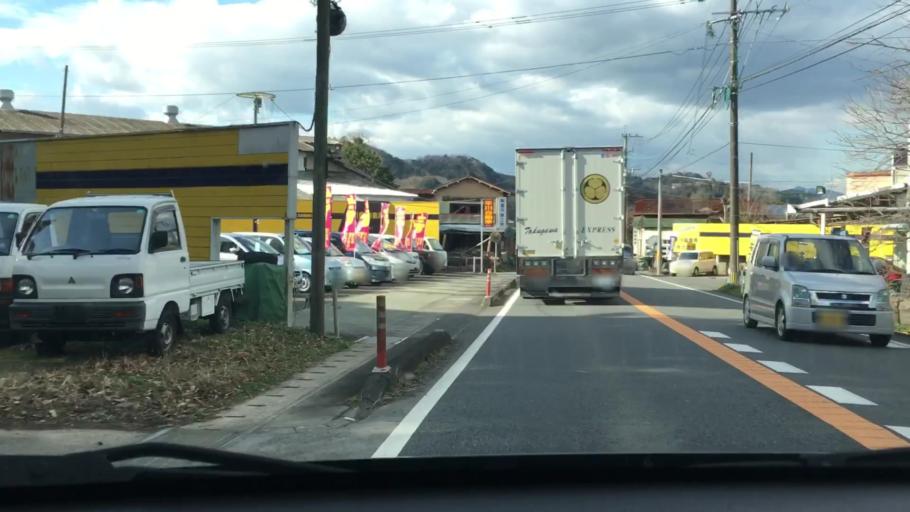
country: JP
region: Oita
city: Usuki
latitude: 33.0309
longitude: 131.6928
